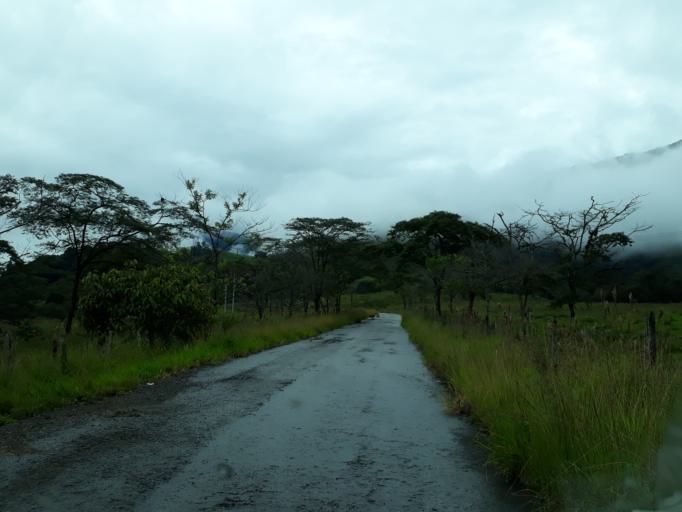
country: CO
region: Cundinamarca
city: Medina
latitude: 4.6827
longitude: -73.3138
